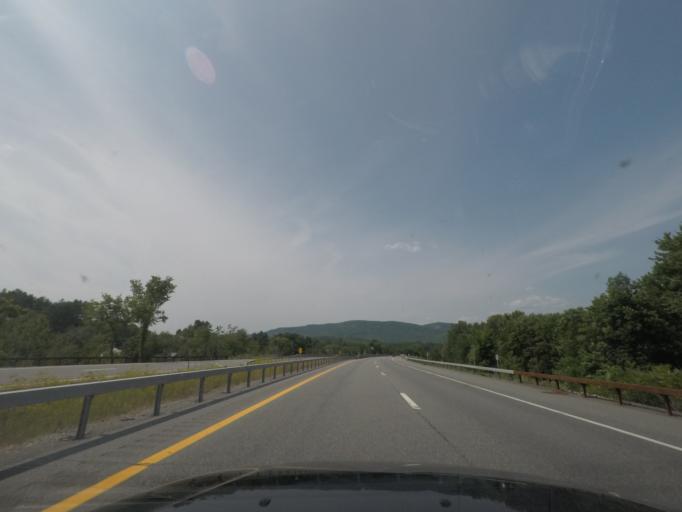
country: US
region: New York
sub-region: Warren County
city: Warrensburg
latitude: 43.7257
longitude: -73.8230
